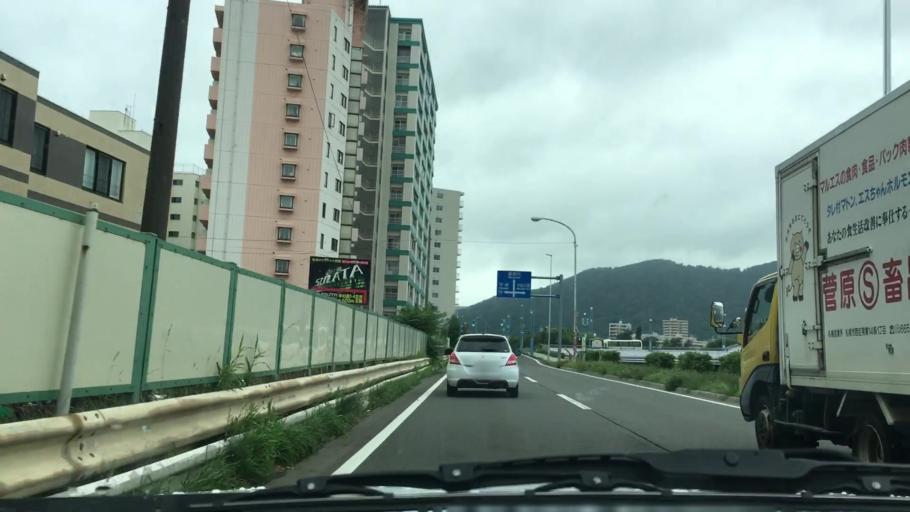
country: JP
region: Hokkaido
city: Sapporo
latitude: 43.0400
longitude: 141.3596
